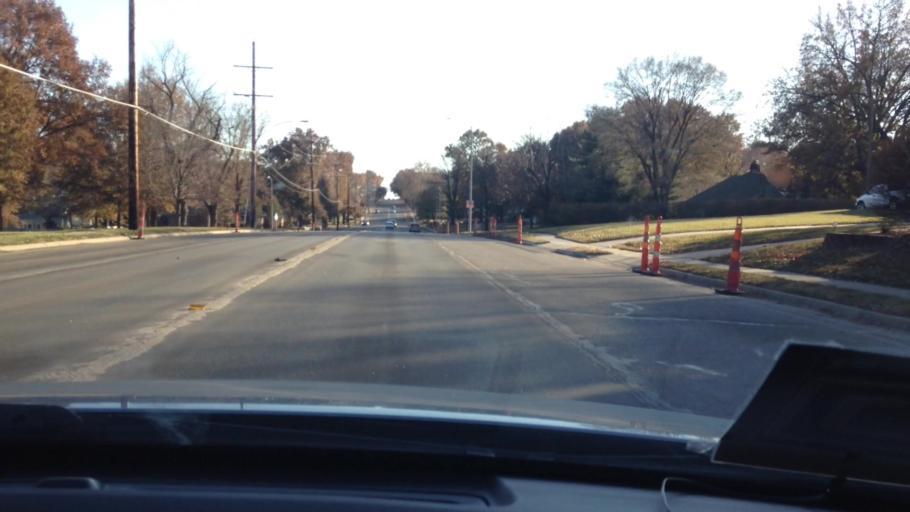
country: US
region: Kansas
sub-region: Johnson County
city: Leawood
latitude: 38.9691
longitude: -94.6304
